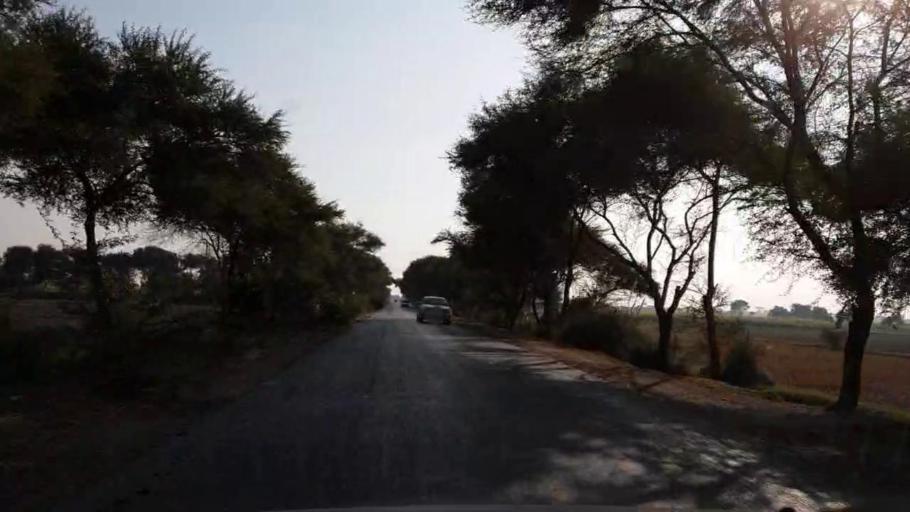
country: PK
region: Sindh
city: Bulri
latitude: 24.8743
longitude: 68.3398
